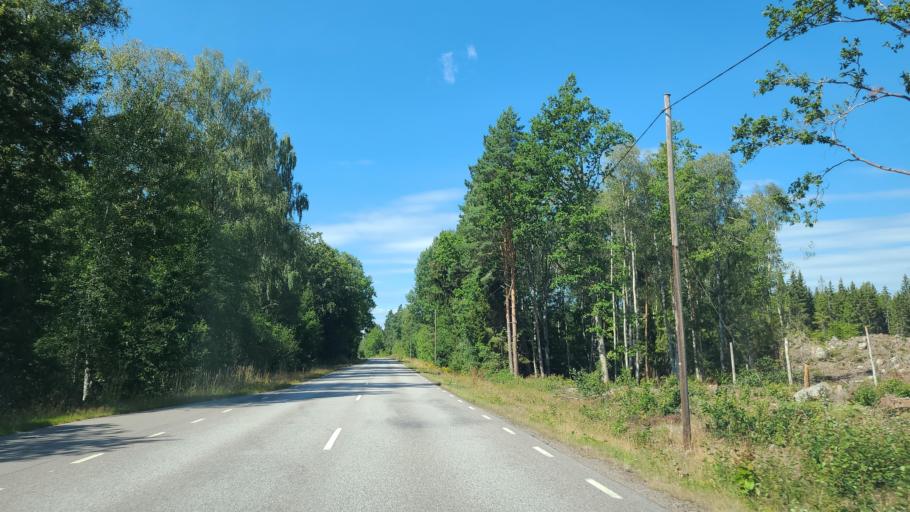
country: SE
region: Kalmar
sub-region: Nybro Kommun
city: Nybro
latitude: 56.5640
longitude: 15.7972
